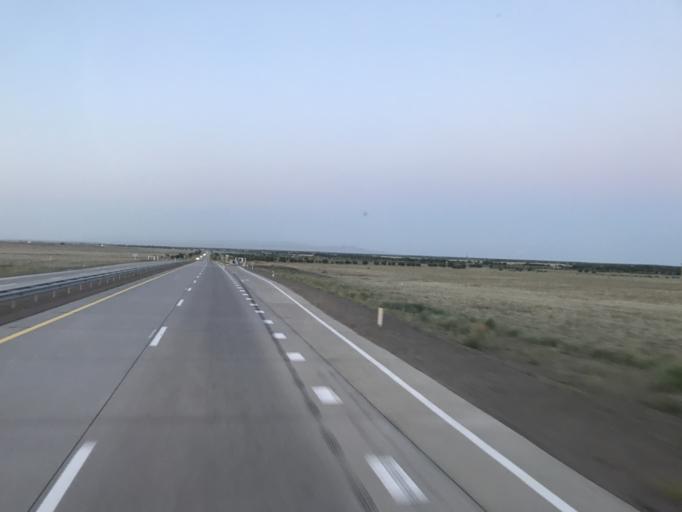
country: KZ
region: Almaty Oblysy
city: Kapshagay
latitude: 43.9716
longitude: 77.3757
